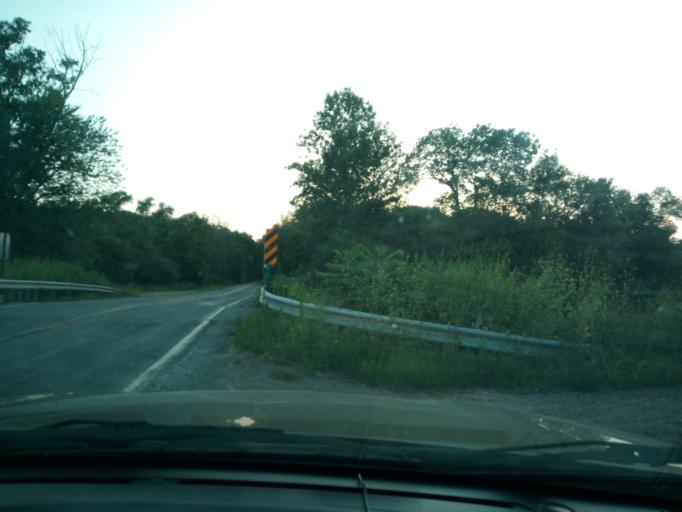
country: US
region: New York
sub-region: Wayne County
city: Clyde
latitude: 43.0213
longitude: -76.7923
